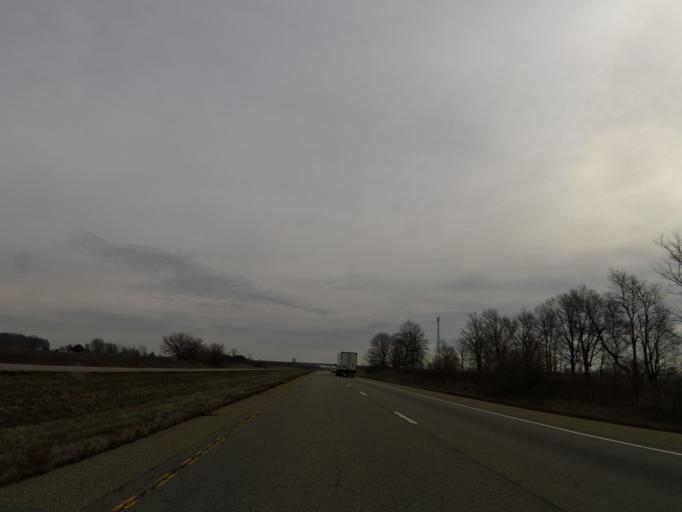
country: US
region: Indiana
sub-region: Fountain County
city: Veedersburg
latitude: 40.1197
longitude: -87.1551
